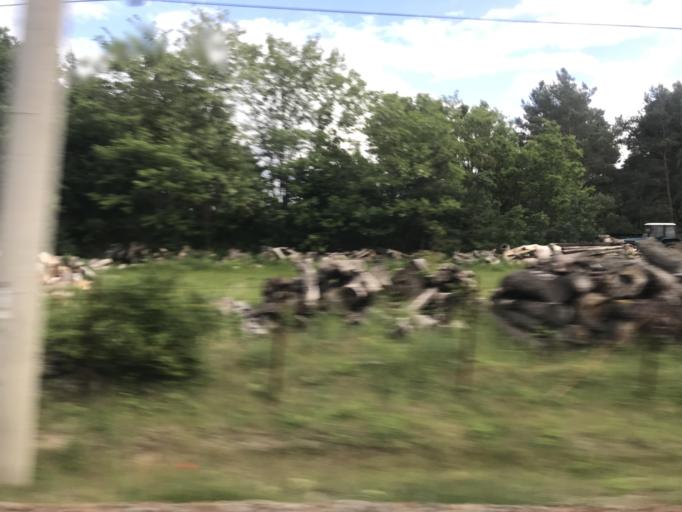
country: DE
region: Brandenburg
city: Luckenwalde
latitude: 52.0754
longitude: 13.1359
